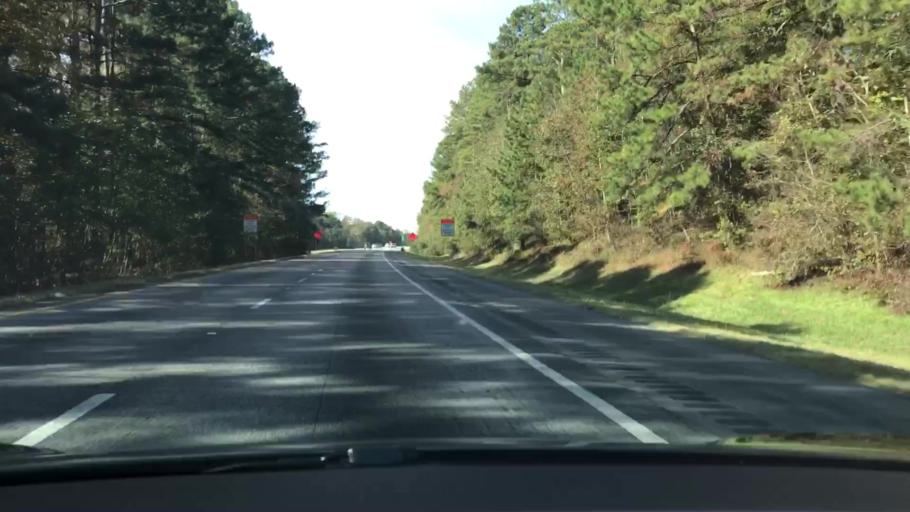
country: US
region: Georgia
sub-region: Morgan County
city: Madison
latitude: 33.5768
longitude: -83.5683
